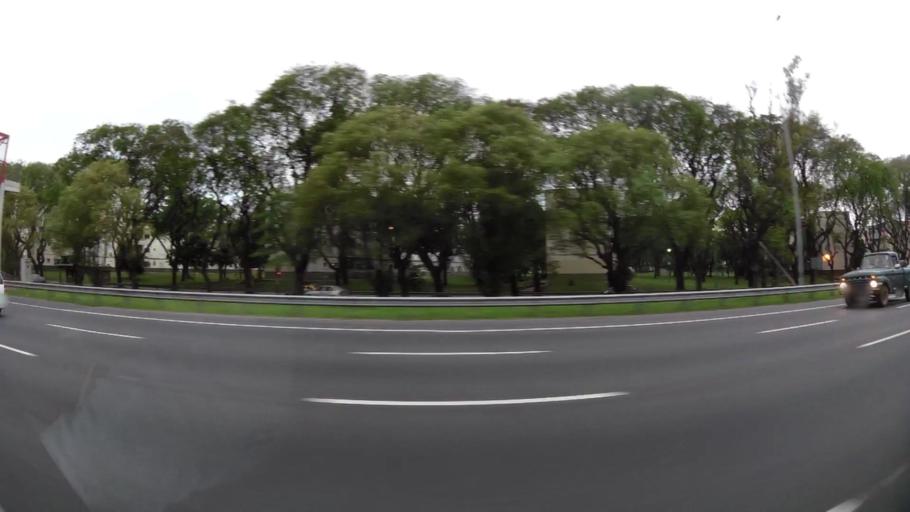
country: AR
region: Buenos Aires
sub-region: Partido de General San Martin
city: General San Martin
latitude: -34.5734
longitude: -58.5112
